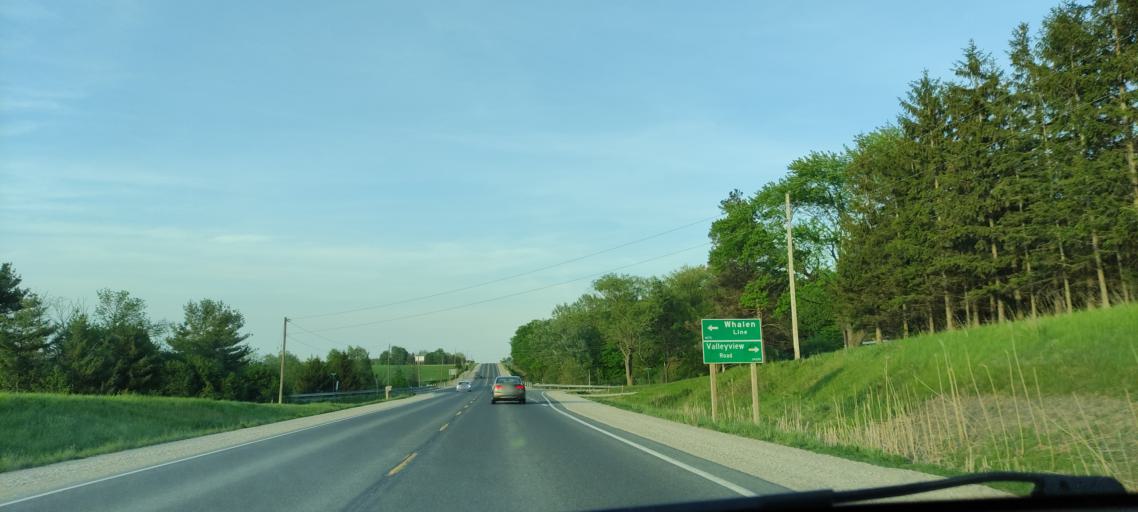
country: CA
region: Ontario
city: London
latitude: 43.2025
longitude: -81.2275
